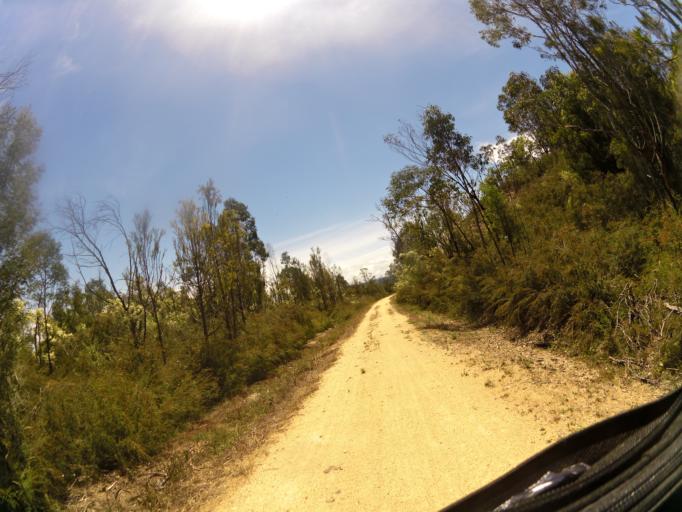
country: AU
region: Victoria
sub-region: East Gippsland
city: Lakes Entrance
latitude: -37.7285
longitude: 147.8531
